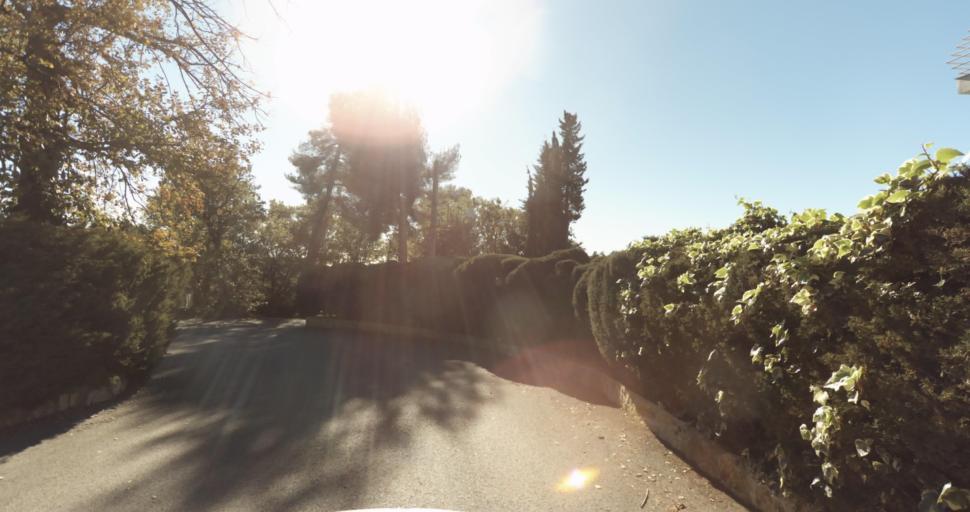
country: FR
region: Provence-Alpes-Cote d'Azur
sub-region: Departement des Alpes-Maritimes
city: Vence
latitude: 43.7205
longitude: 7.1007
